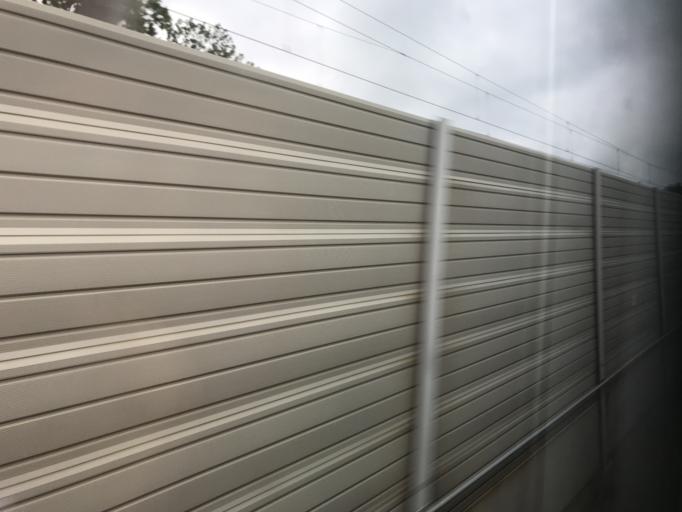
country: DE
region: Bavaria
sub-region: Upper Bavaria
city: Maisach
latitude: 48.2131
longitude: 11.2955
